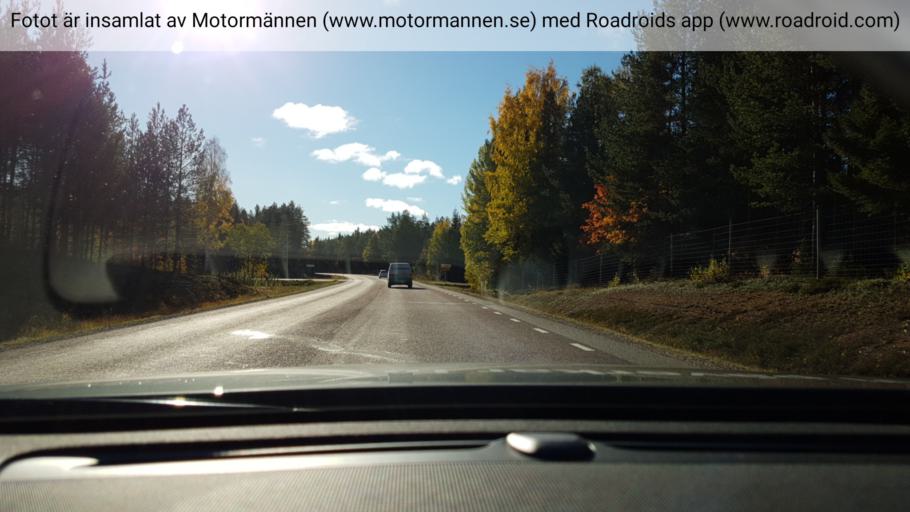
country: SE
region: Vaesterbotten
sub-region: Skelleftea Kommun
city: Burea
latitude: 64.6171
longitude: 21.1791
